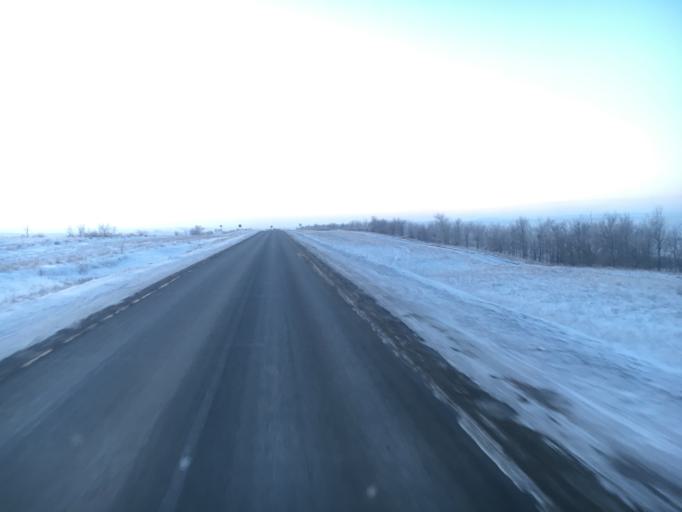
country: KZ
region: Aqtoebe
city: Aqtobe
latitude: 50.2846
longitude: 57.7319
